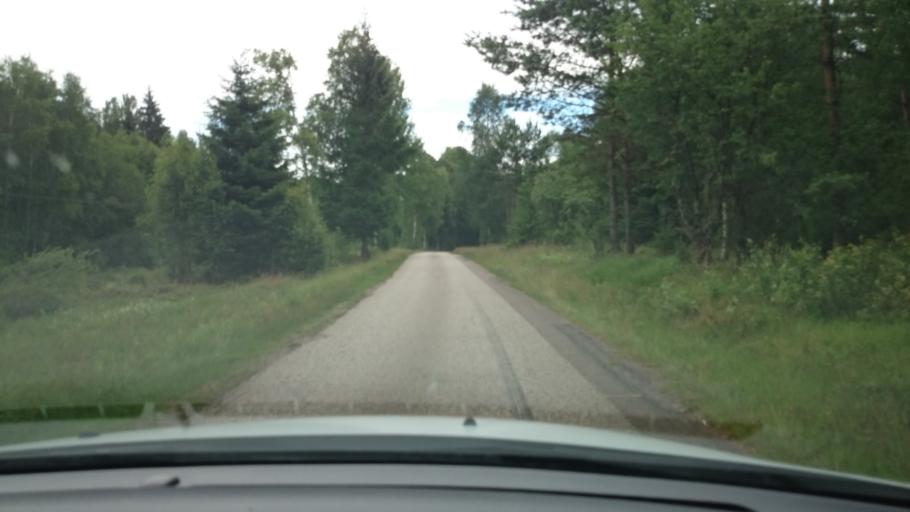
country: SE
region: Halland
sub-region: Hylte Kommun
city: Hyltebruk
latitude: 56.9797
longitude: 13.2101
